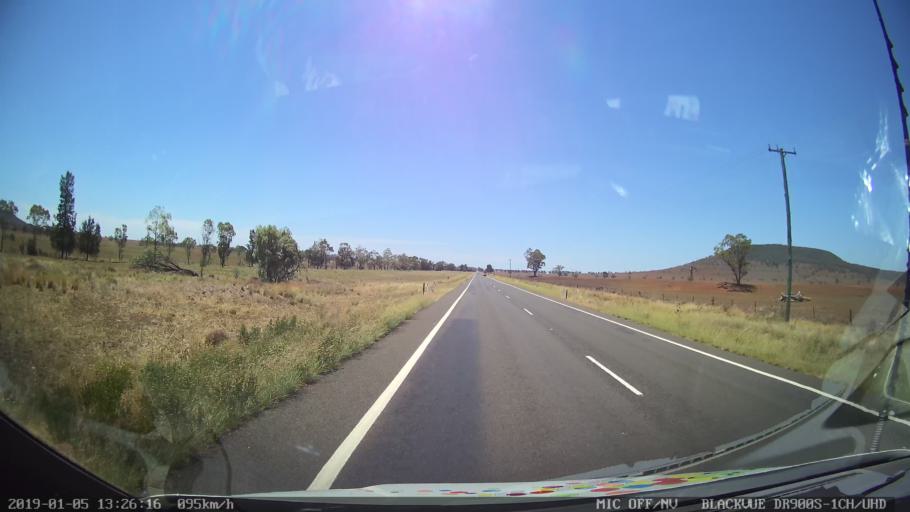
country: AU
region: New South Wales
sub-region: Gunnedah
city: Gunnedah
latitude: -31.0544
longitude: 150.0133
